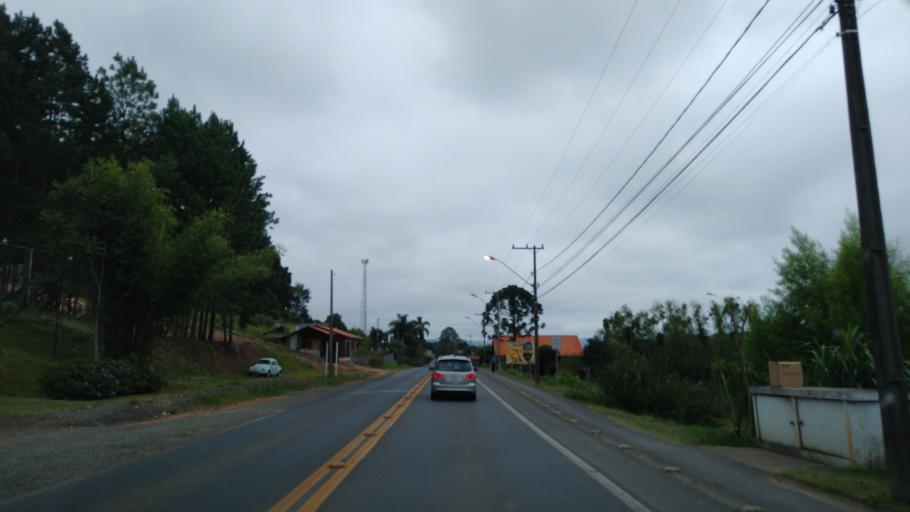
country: BR
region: Santa Catarina
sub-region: Porto Uniao
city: Porto Uniao
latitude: -26.2741
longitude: -51.0544
